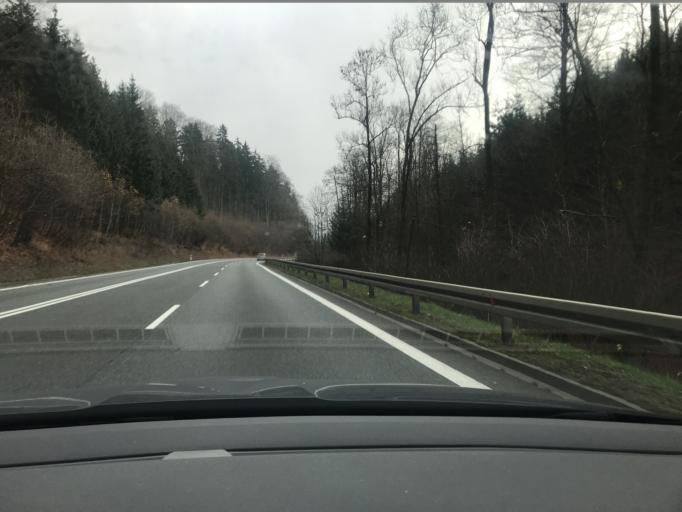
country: PL
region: Lower Silesian Voivodeship
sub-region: Powiat klodzki
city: Lewin Klodzki
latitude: 50.4104
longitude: 16.3238
